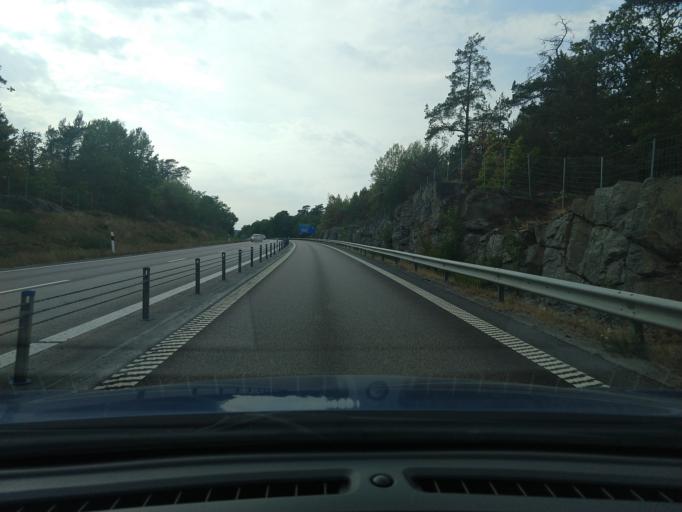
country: SE
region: Blekinge
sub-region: Karlskrona Kommun
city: Rodeby
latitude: 56.2083
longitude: 15.6187
